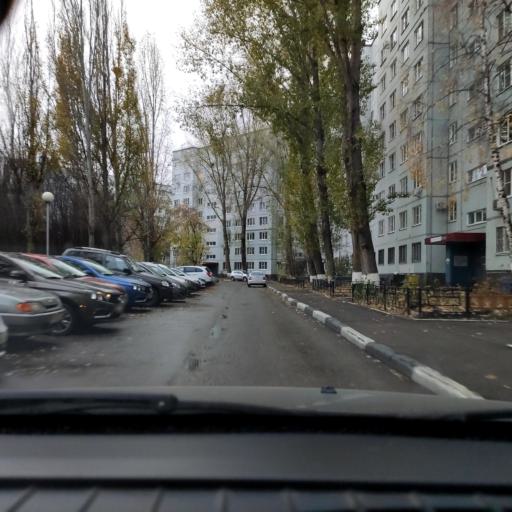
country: RU
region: Samara
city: Tol'yatti
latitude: 53.5316
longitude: 49.3243
